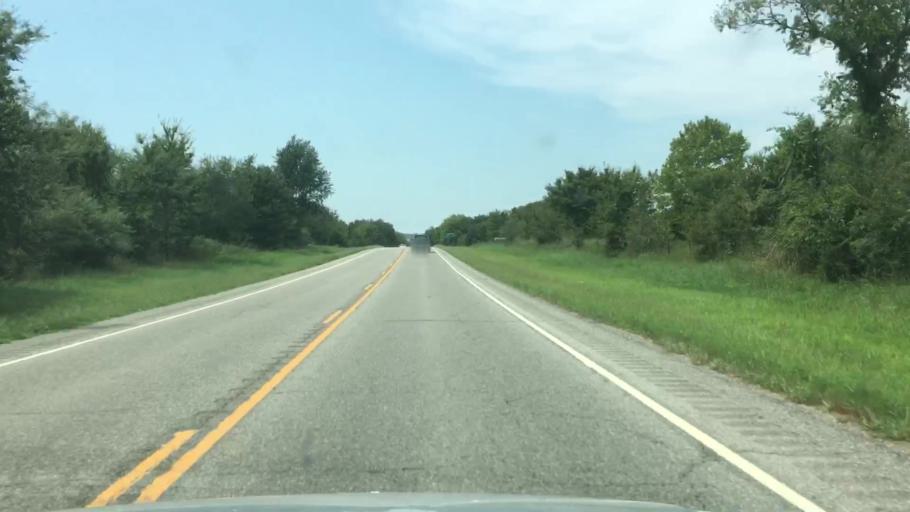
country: US
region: Oklahoma
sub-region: Muskogee County
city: Fort Gibson
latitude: 35.9370
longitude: -95.2047
